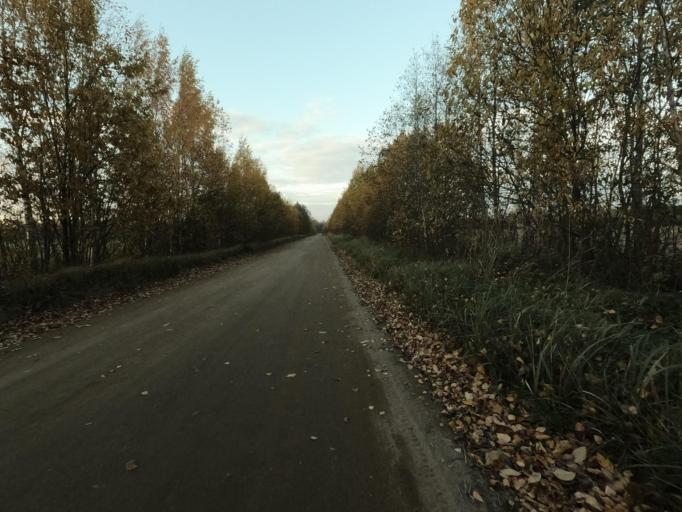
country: RU
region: Leningrad
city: Mga
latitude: 59.8029
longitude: 31.2006
